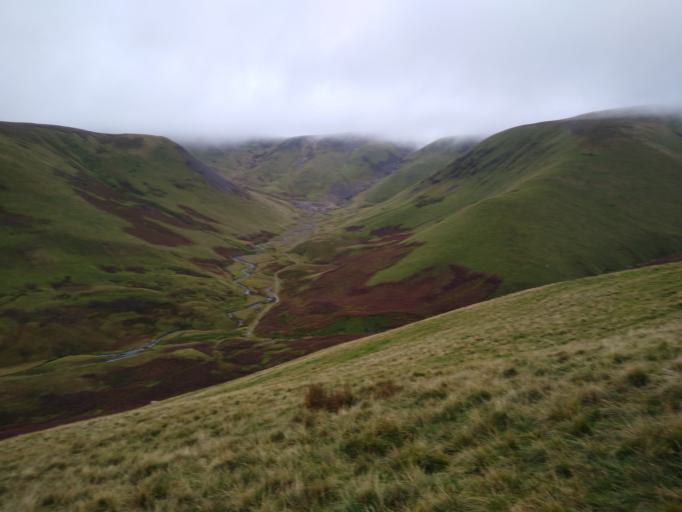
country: GB
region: England
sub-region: Cumbria
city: Keswick
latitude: 54.7097
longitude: -3.0929
